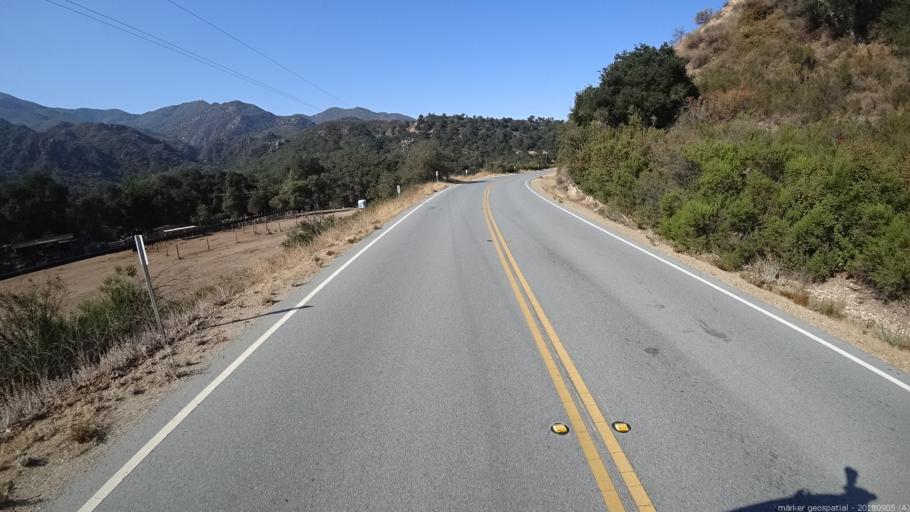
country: US
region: California
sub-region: Monterey County
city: Greenfield
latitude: 36.2408
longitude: -121.4343
